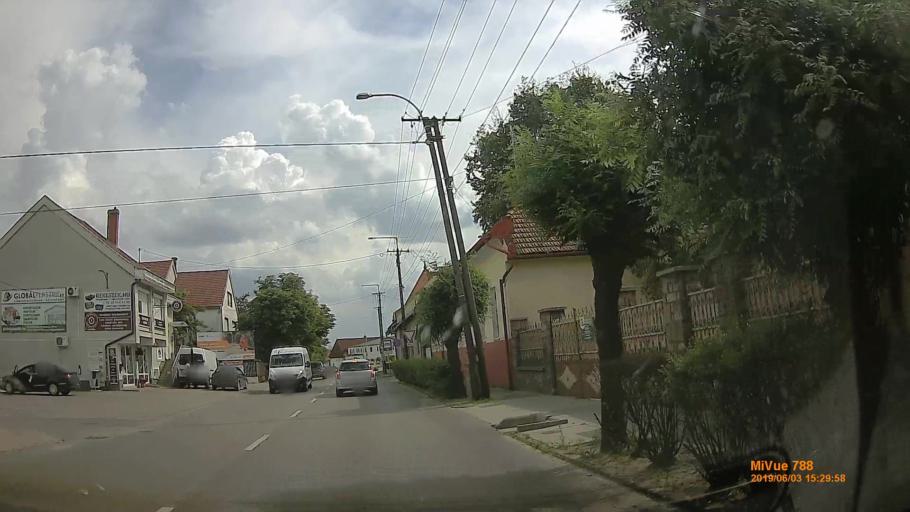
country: HU
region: Bacs-Kiskun
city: Soltvadkert
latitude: 46.5821
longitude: 19.3937
